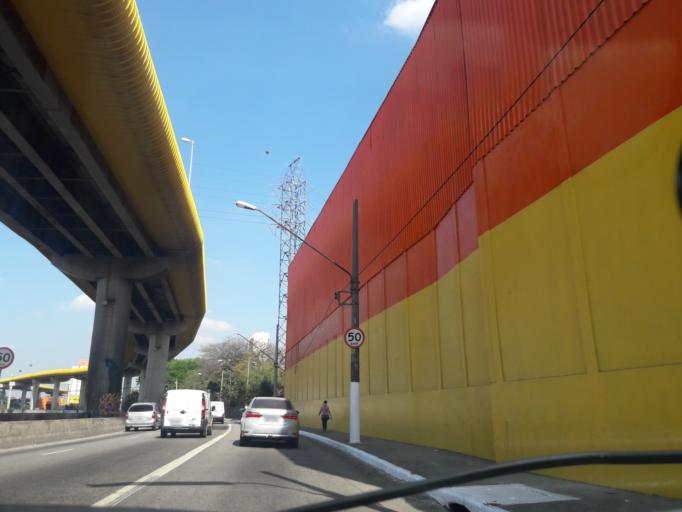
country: BR
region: Sao Paulo
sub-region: Sao Paulo
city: Sao Paulo
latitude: -23.5835
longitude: -46.5999
